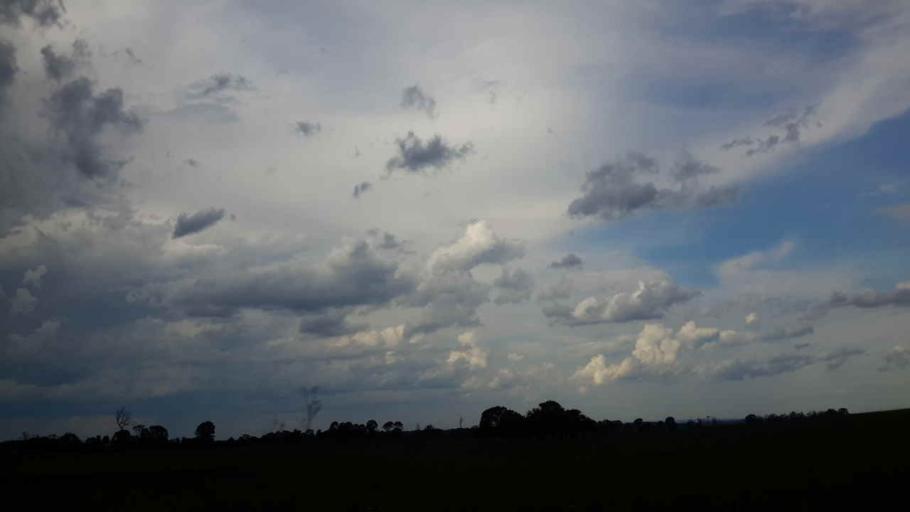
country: AU
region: New South Wales
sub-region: Liverpool
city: Luddenham
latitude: -33.8495
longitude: 150.6893
